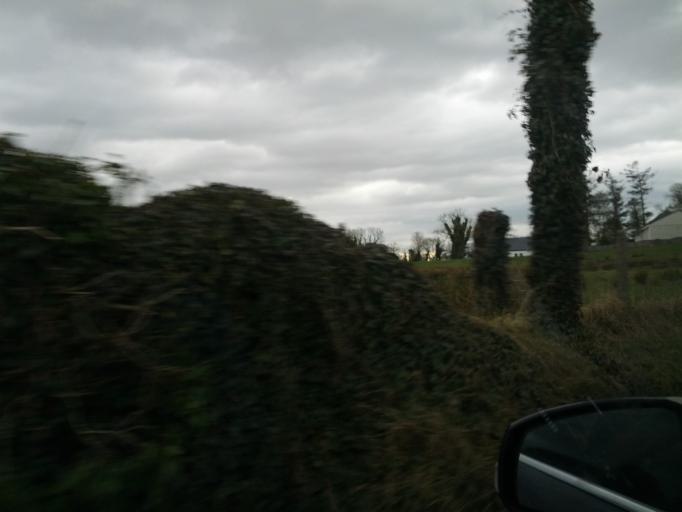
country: IE
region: Connaught
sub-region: County Galway
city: Athenry
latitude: 53.3729
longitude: -8.6388
